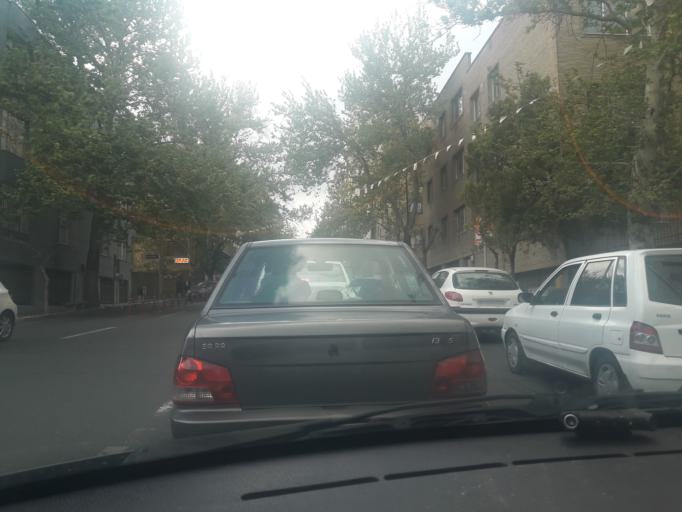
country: IR
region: Tehran
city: Tehran
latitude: 35.7422
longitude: 51.4052
